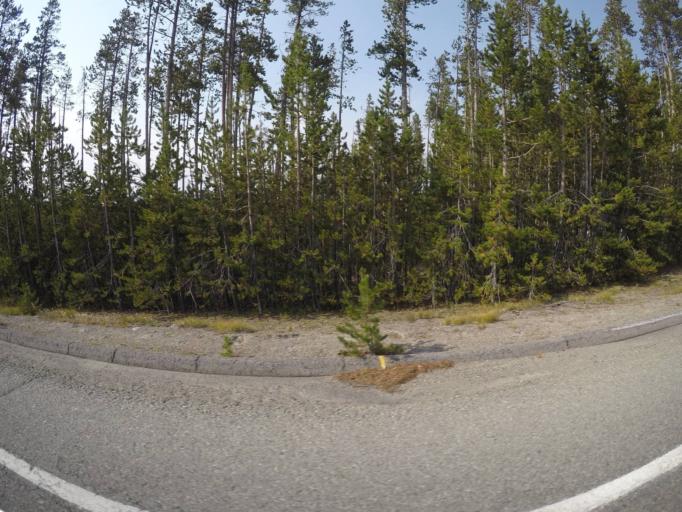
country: US
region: Montana
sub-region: Gallatin County
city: West Yellowstone
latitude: 44.7189
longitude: -110.6536
